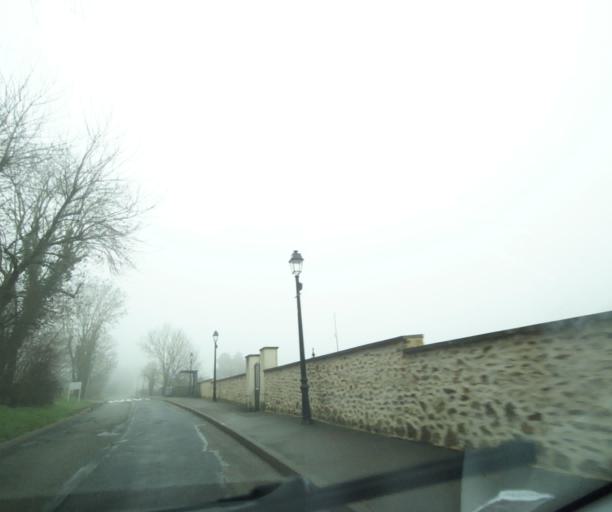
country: FR
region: Ile-de-France
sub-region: Departement de Seine-et-Marne
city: Longperrier
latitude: 49.0524
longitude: 2.6668
